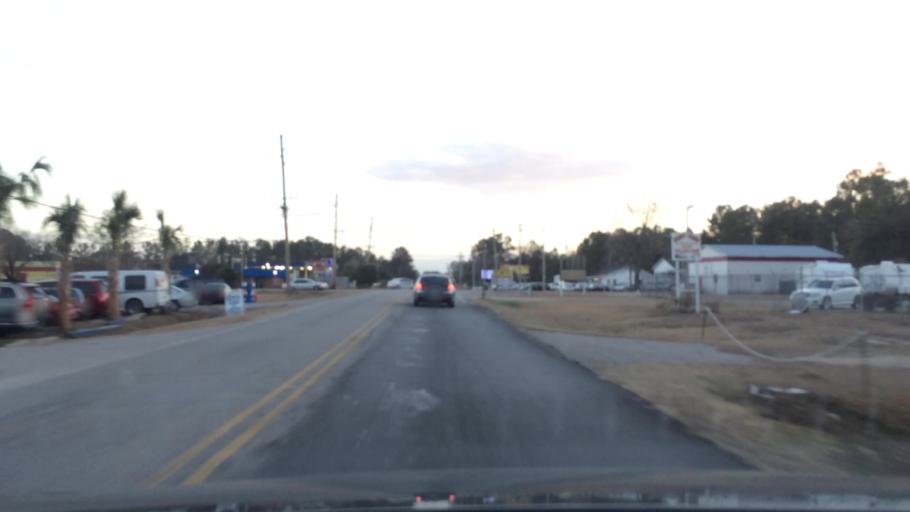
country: US
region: South Carolina
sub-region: Horry County
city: Red Hill
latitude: 33.8052
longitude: -79.0185
